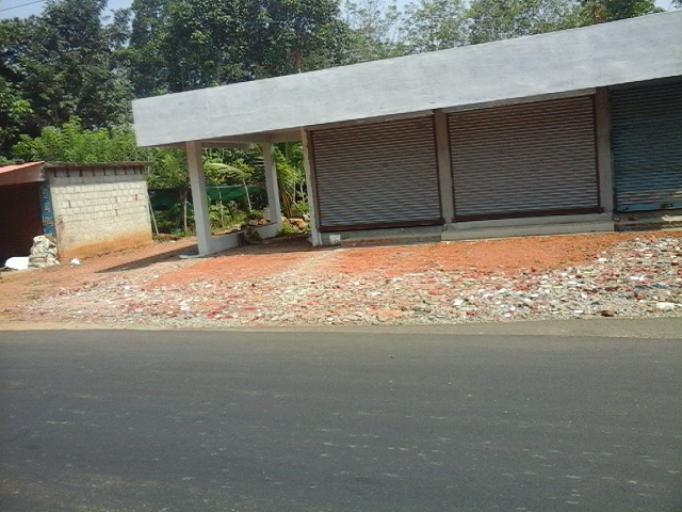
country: IN
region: Kerala
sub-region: Kottayam
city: Erattupetta
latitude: 9.5860
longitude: 76.7410
